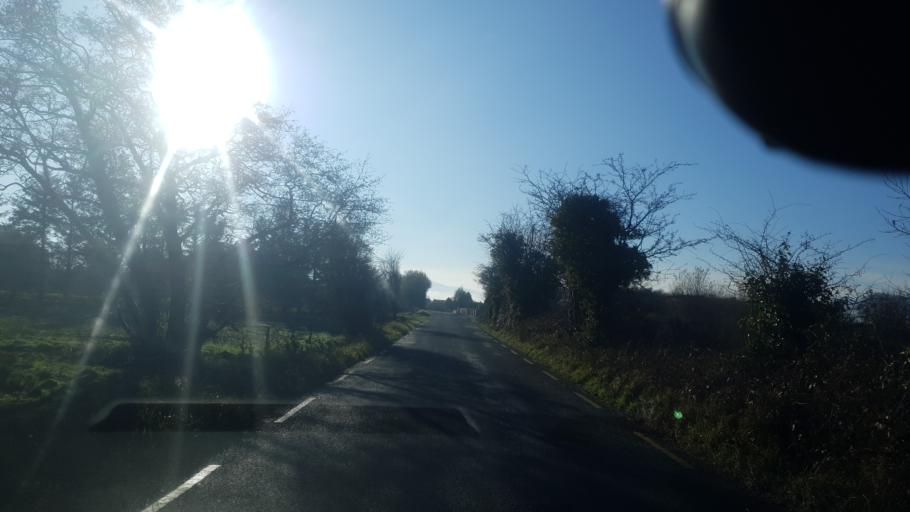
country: IE
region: Munster
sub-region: Ciarrai
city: Cill Airne
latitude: 52.1045
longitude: -9.4722
